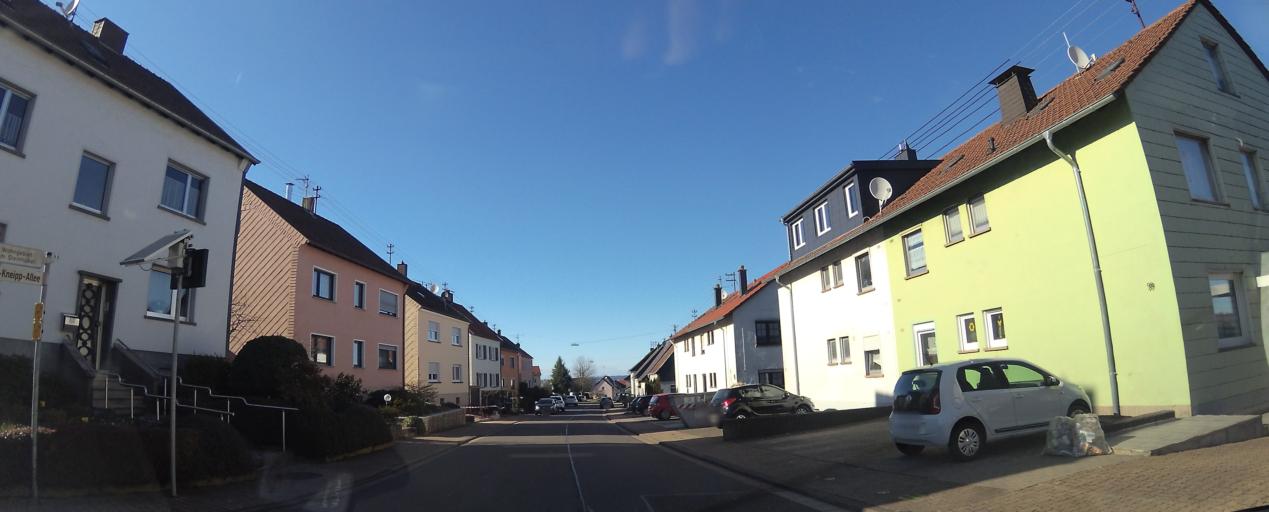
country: DE
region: Saarland
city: Riegelsberg
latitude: 49.3009
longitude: 6.9307
